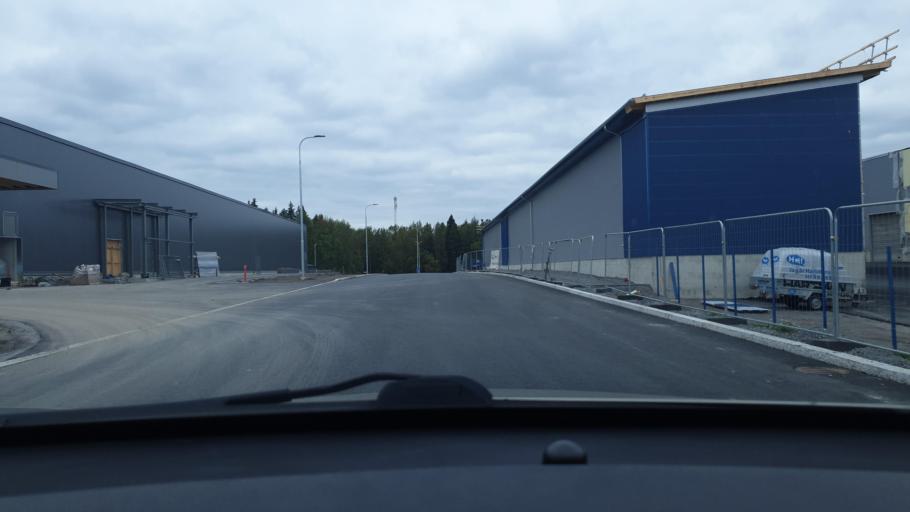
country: FI
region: Ostrobothnia
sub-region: Vaasa
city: Teeriniemi
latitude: 63.0727
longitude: 21.7007
